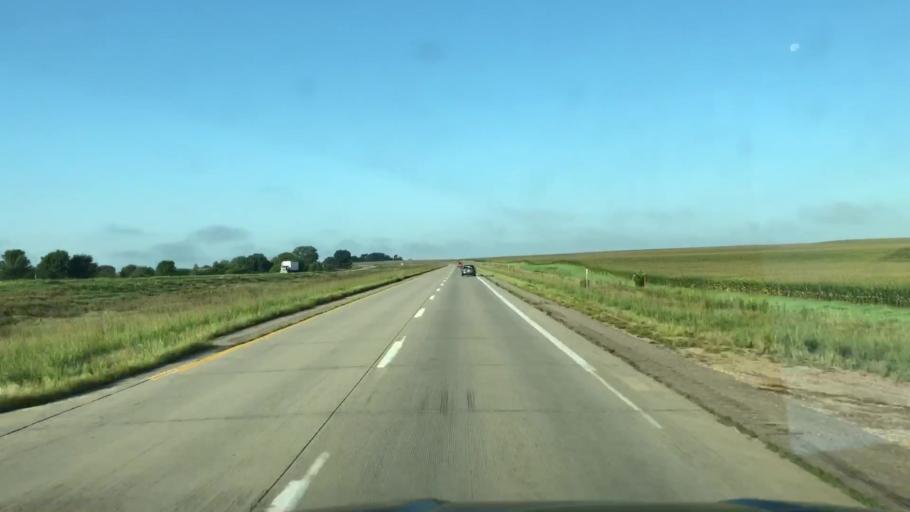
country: US
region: Iowa
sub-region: Sioux County
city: Orange City
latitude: 42.9233
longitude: -96.0655
